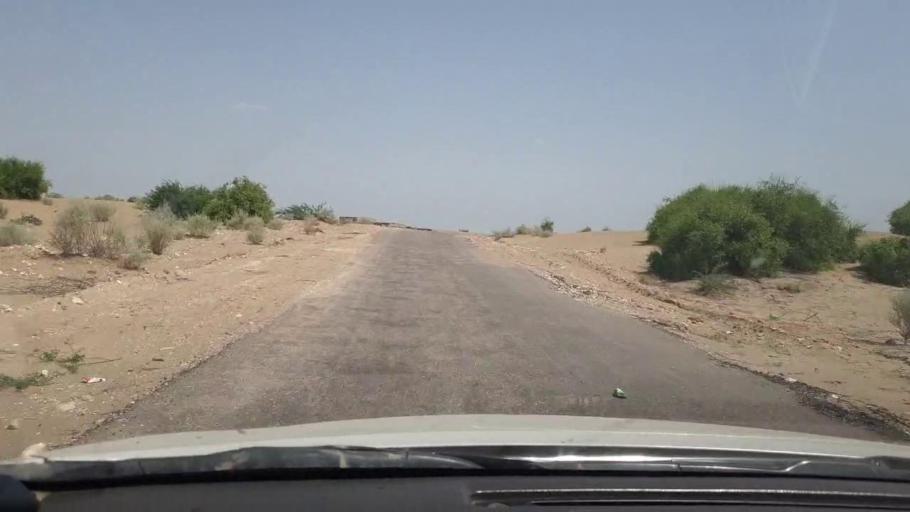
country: PK
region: Sindh
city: Rohri
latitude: 27.4920
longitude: 69.0500
